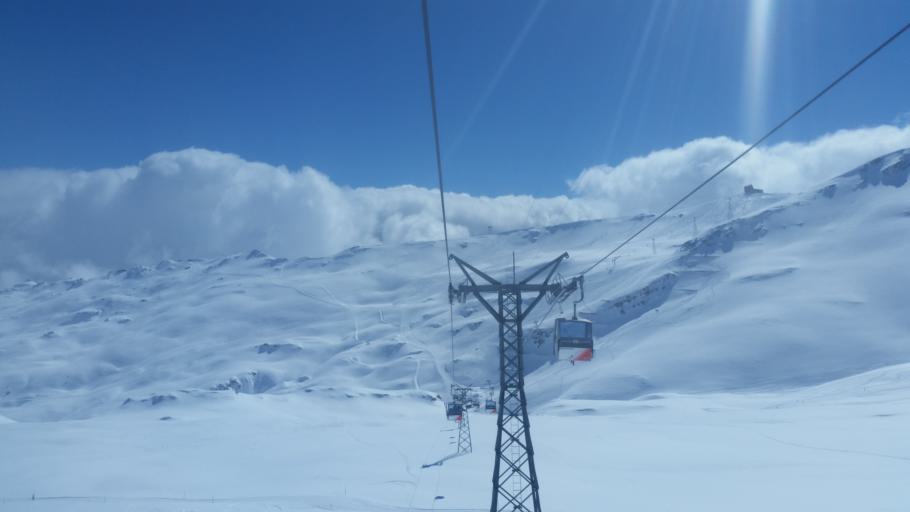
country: CH
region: Grisons
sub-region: Surselva District
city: Ilanz
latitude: 46.8602
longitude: 9.1852
